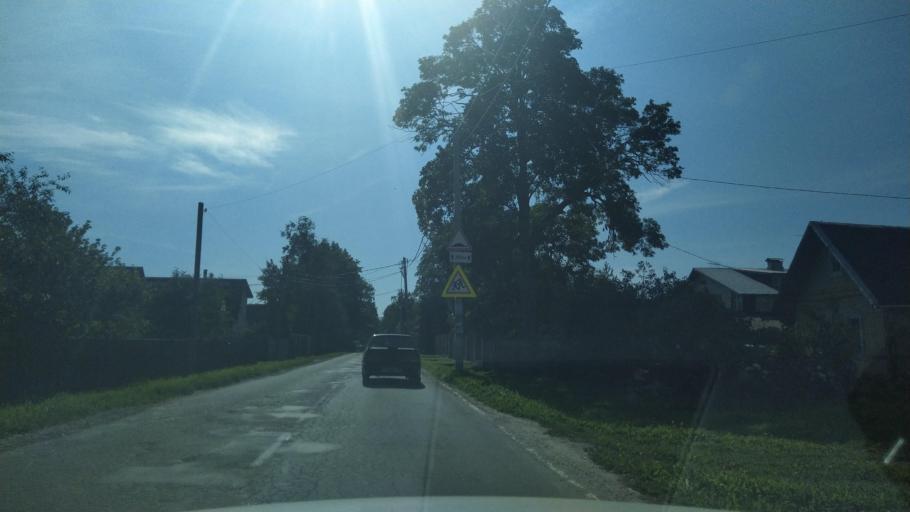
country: RU
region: Leningrad
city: Siverskiy
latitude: 59.3295
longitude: 30.0366
